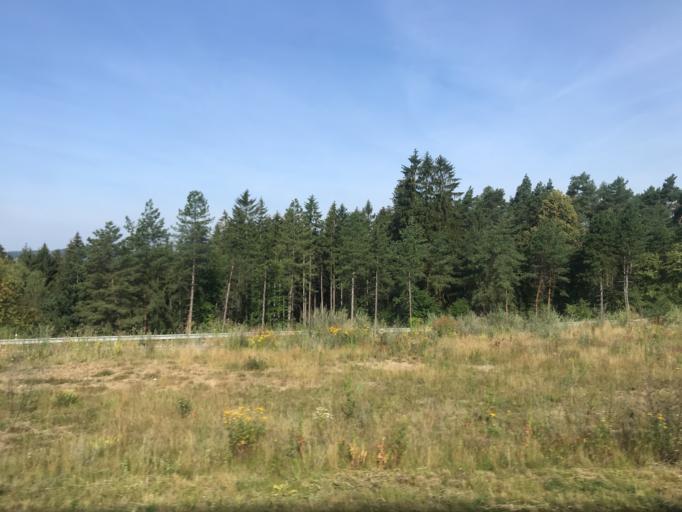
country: CZ
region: Jihocesky
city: Chotoviny
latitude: 49.5020
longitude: 14.6557
